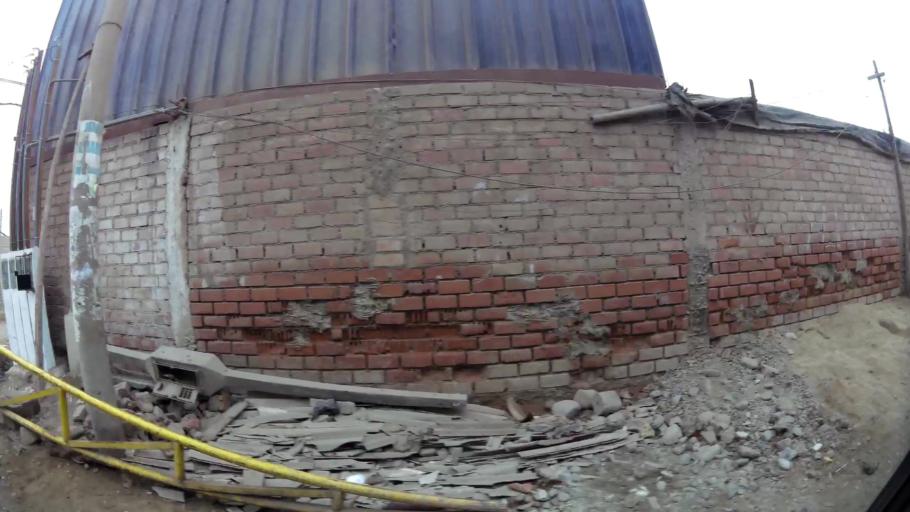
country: PE
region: Lima
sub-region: Lima
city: Urb. Santo Domingo
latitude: -11.8957
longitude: -77.0629
